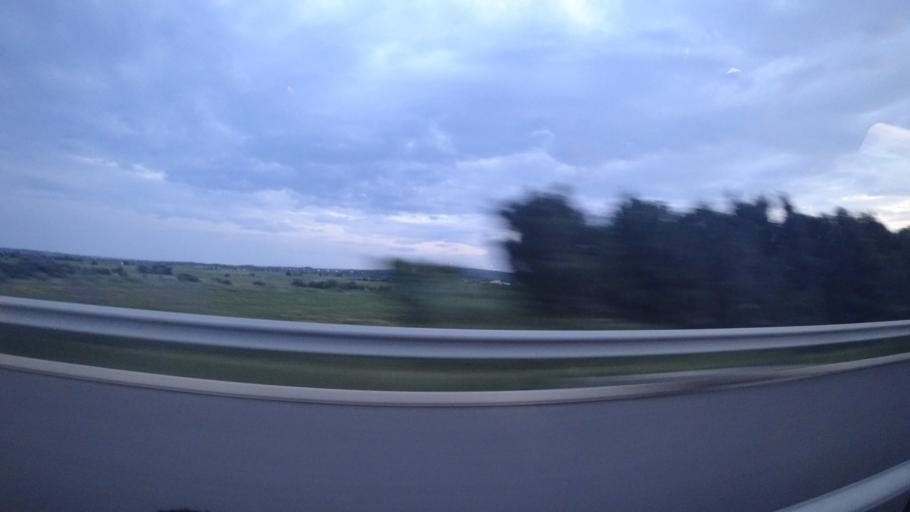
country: FR
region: Languedoc-Roussillon
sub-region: Departement de l'Aude
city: Leucate
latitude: 42.9379
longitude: 2.9840
